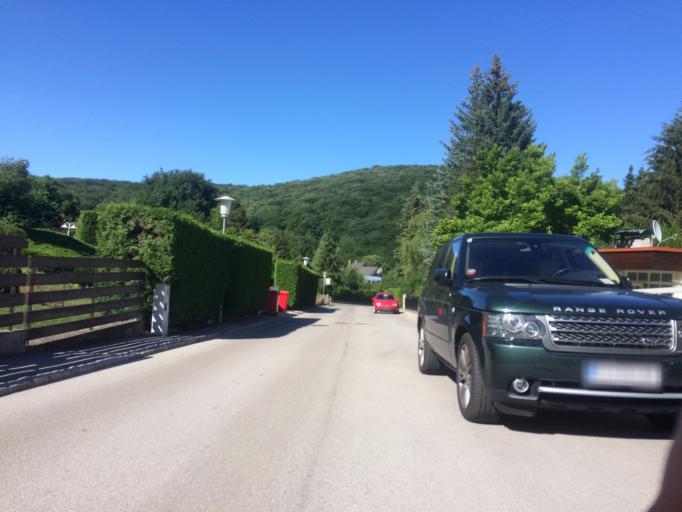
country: AT
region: Lower Austria
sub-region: Politischer Bezirk Wien-Umgebung
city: Purkersdorf
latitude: 48.2112
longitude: 16.1694
